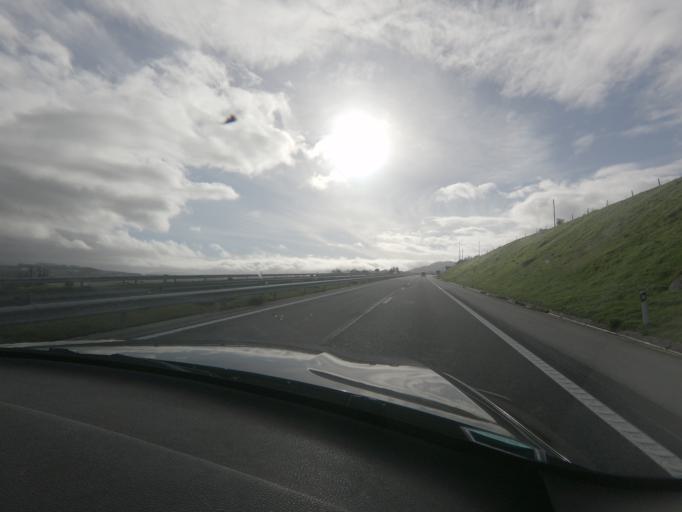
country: PT
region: Viseu
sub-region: Lamego
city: Lamego
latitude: 41.0852
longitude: -7.7905
